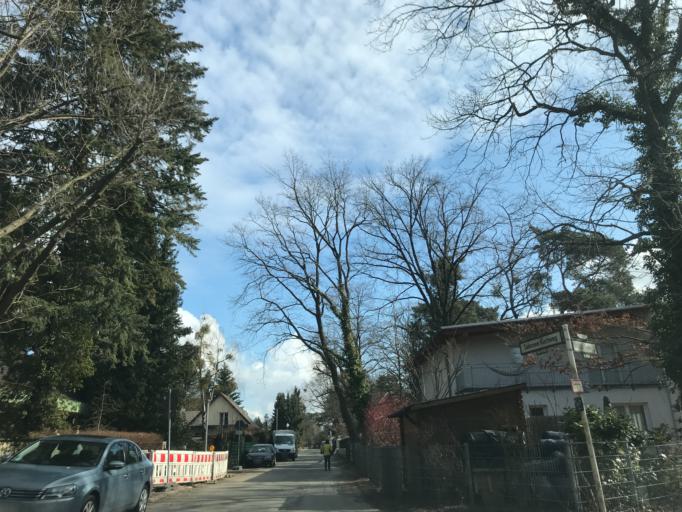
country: DE
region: Berlin
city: Kladow
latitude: 52.4493
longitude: 13.1401
